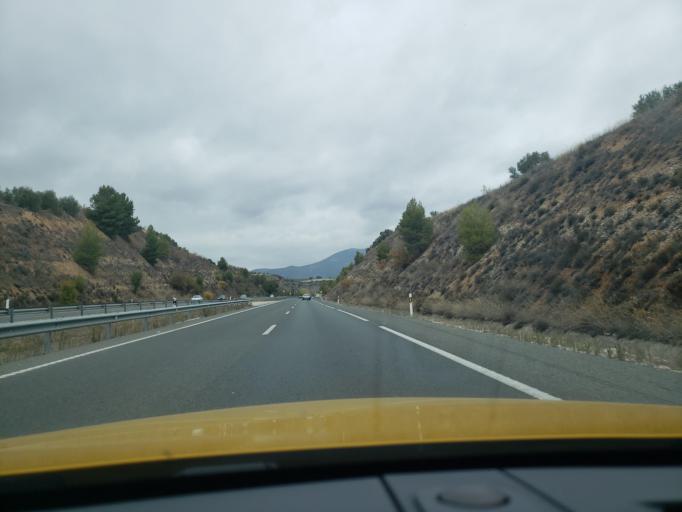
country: ES
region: Andalusia
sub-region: Provincia de Granada
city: Calicasas
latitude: 37.2962
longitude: -3.6570
